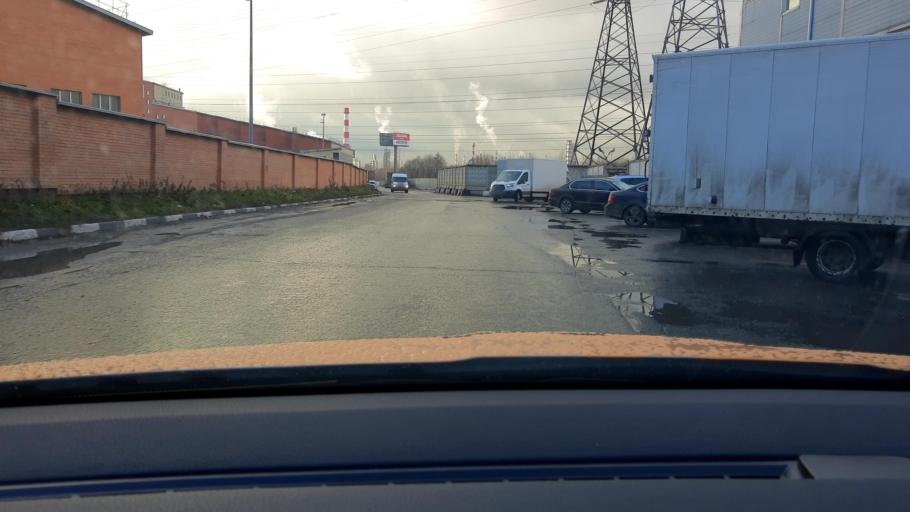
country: RU
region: Moskovskaya
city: Kotel'niki
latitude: 55.6457
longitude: 37.8341
